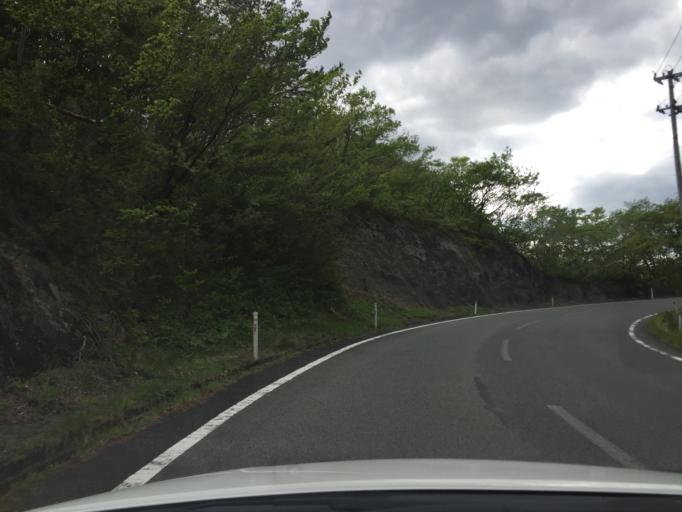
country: JP
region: Miyagi
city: Marumori
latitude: 37.7172
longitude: 140.8378
